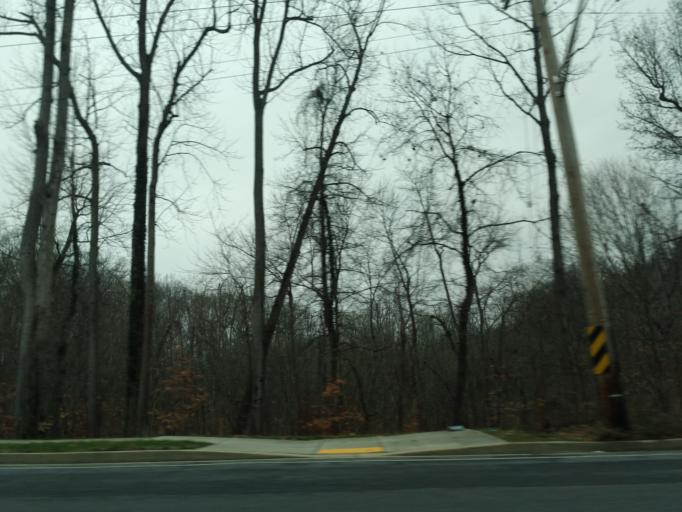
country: US
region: Maryland
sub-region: Calvert County
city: Chesapeake Beach
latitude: 38.6782
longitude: -76.5358
